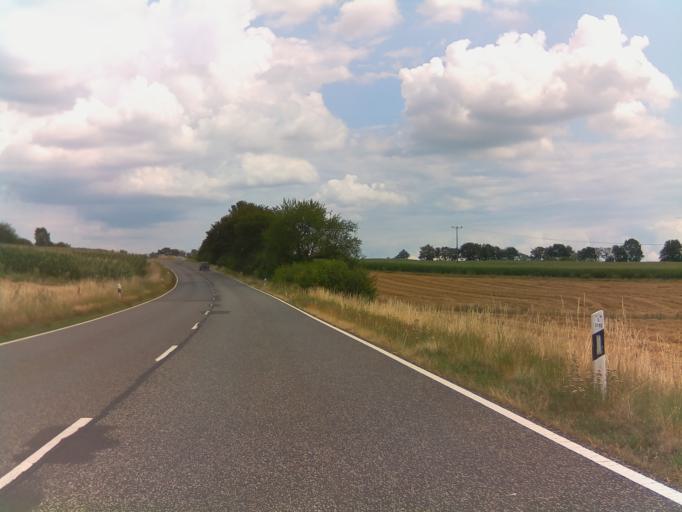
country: DE
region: Hesse
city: Gedern
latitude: 50.4123
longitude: 9.2183
